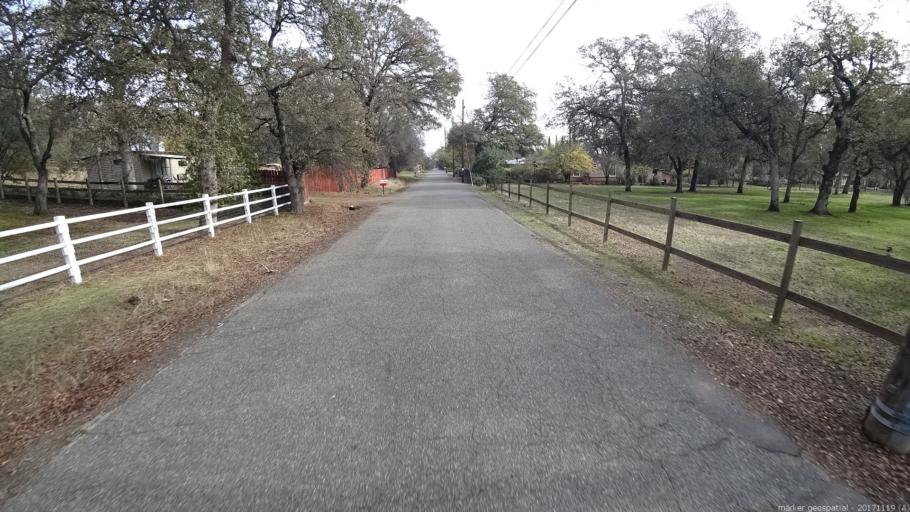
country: US
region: California
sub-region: Shasta County
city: Anderson
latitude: 40.4766
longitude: -122.2982
